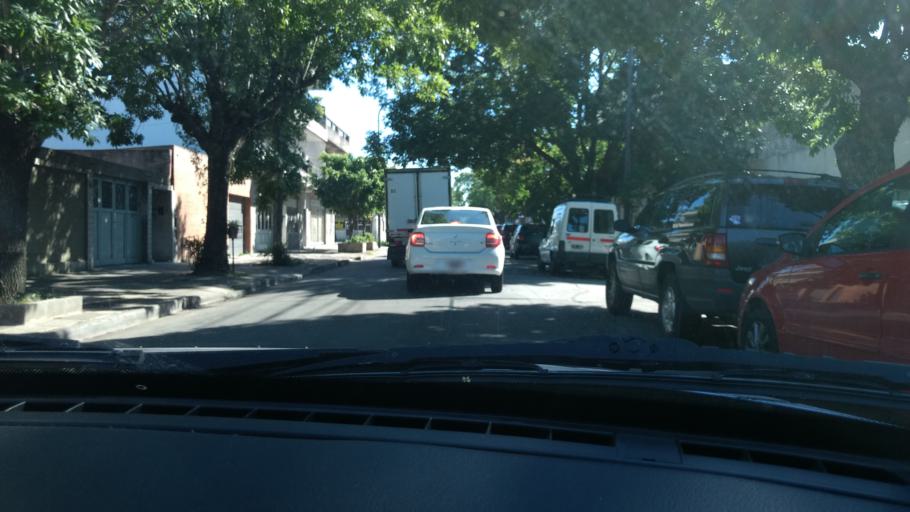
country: AR
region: Buenos Aires F.D.
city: Villa Santa Rita
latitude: -34.6176
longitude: -58.5156
